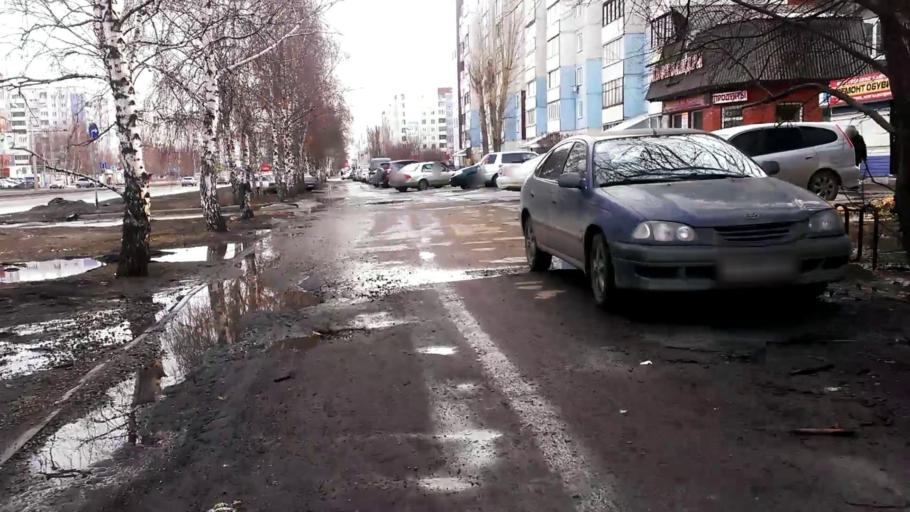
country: RU
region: Altai Krai
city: Novoaltaysk
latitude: 53.3754
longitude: 83.9214
